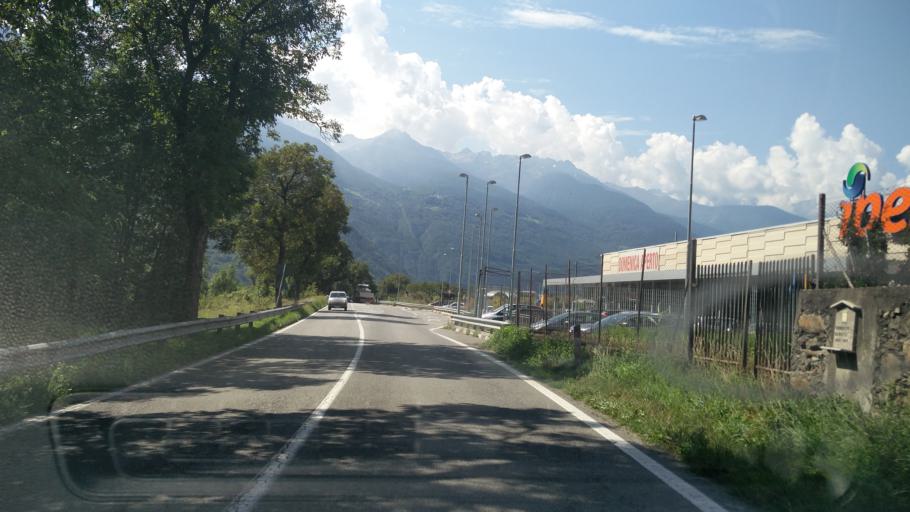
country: IT
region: Lombardy
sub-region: Provincia di Sondrio
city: Bianzone
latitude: 46.1897
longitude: 10.1228
